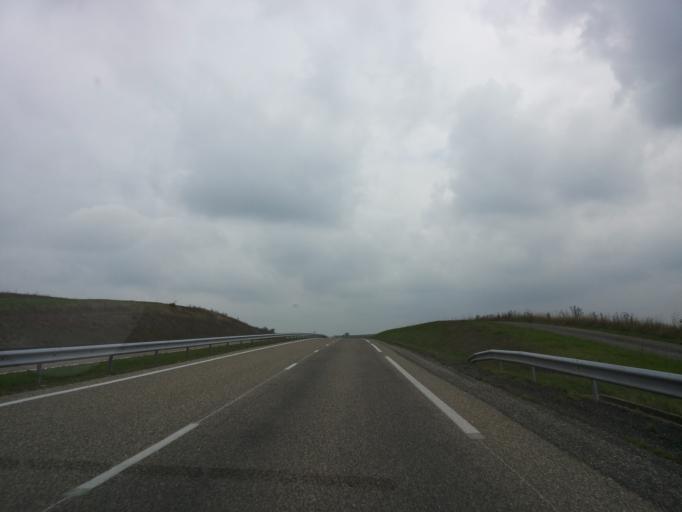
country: FR
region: Lorraine
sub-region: Departement de la Moselle
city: Dieuze
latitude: 48.7338
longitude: 6.6864
